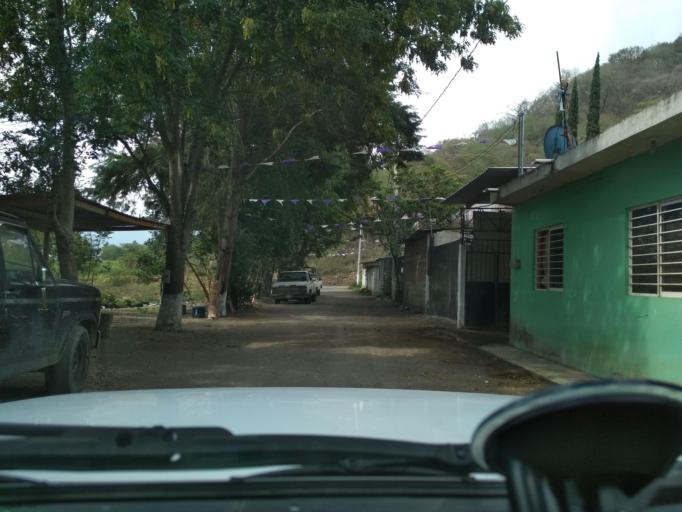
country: MX
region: Veracruz
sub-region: Nogales
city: Taza de Agua Ojo Zarco
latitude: 18.7810
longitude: -97.2008
